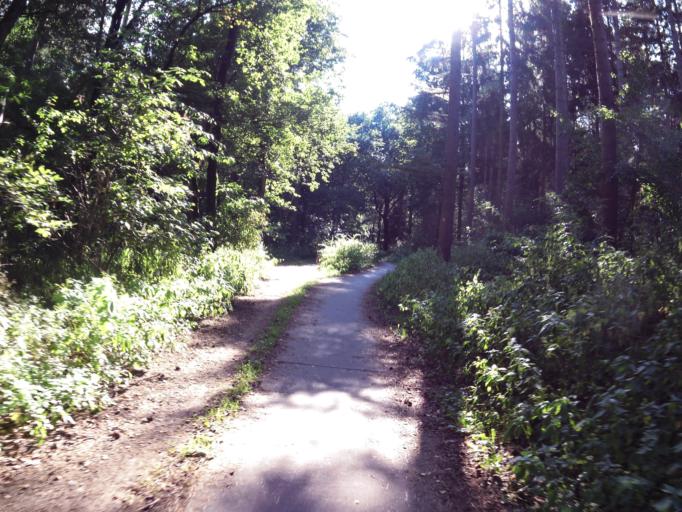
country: NL
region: Gelderland
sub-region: Gemeente Montferland
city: s-Heerenberg
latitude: 51.8806
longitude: 6.2075
